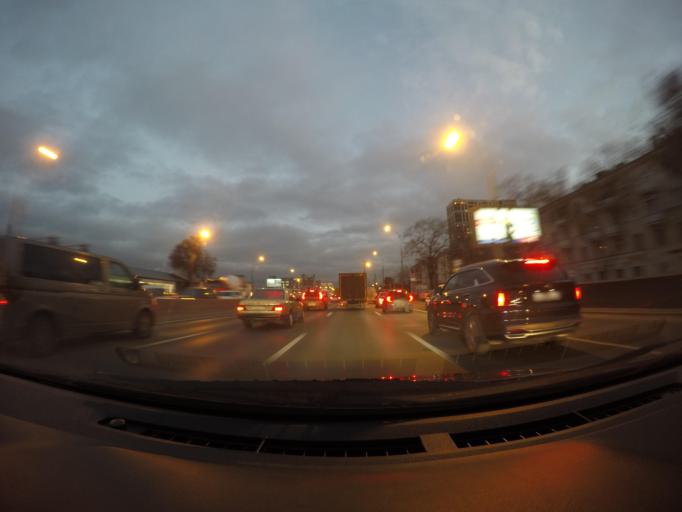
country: RU
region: Moscow
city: Kolomenskoye
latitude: 55.6440
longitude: 37.6759
